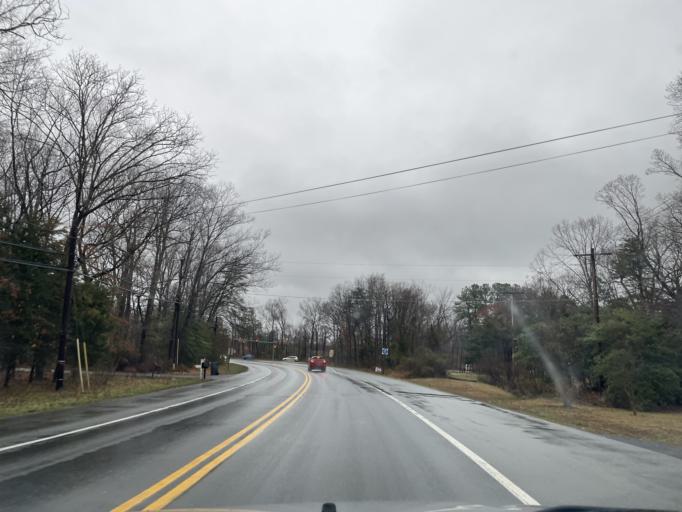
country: US
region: Maryland
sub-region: Charles County
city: La Plata
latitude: 38.5306
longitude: -76.9580
